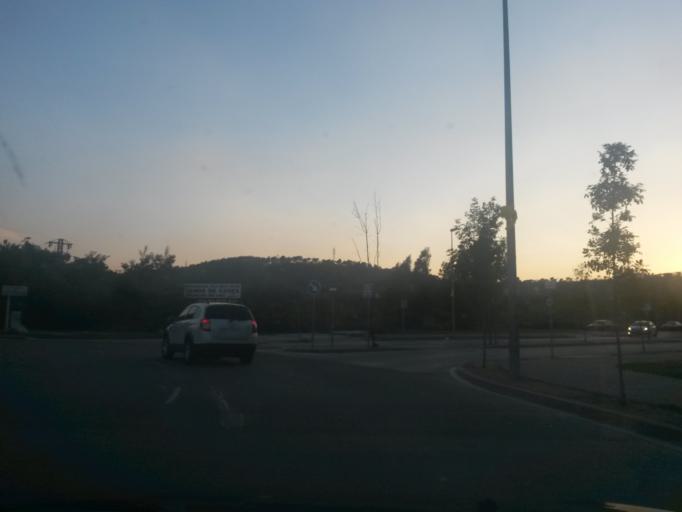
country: ES
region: Catalonia
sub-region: Provincia de Girona
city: Sarria de Ter
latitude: 42.0092
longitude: 2.8168
